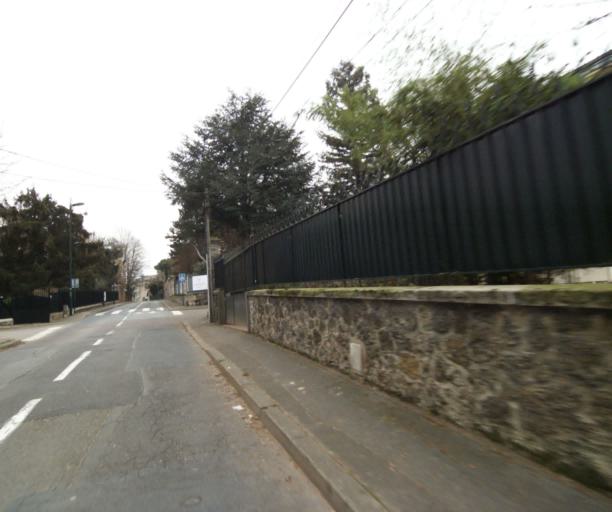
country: FR
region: Ile-de-France
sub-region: Departement des Hauts-de-Seine
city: Garches
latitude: 48.8394
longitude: 2.1799
